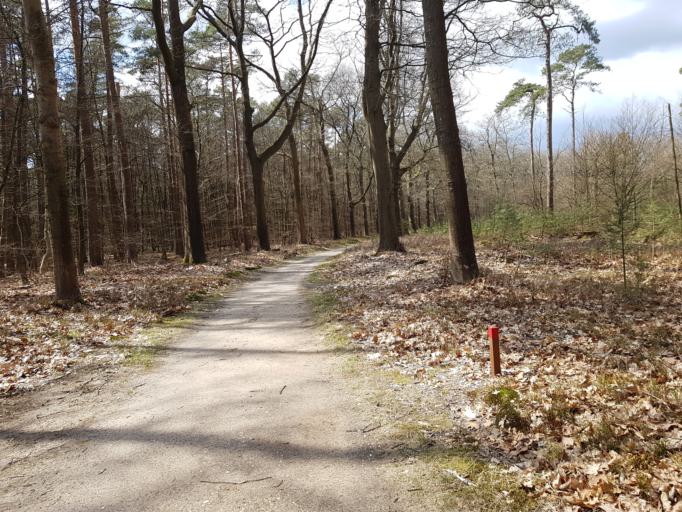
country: NL
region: Gelderland
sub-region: Gemeente Apeldoorn
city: Apeldoorn
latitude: 52.2423
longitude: 5.9339
